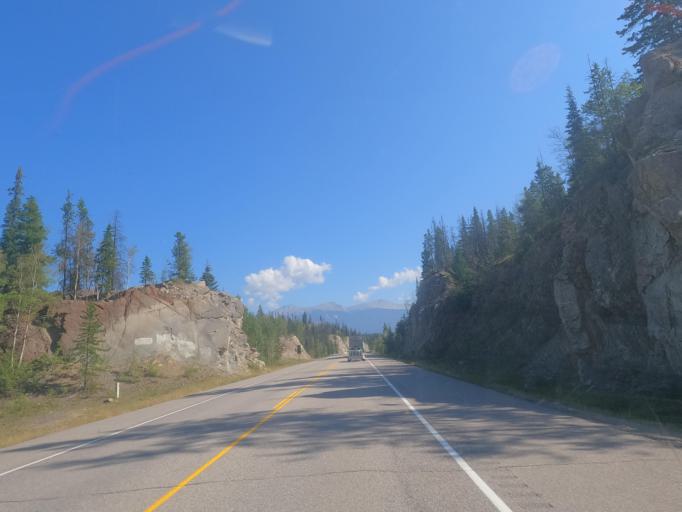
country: CA
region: Alberta
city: Jasper Park Lodge
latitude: 52.8616
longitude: -118.1099
